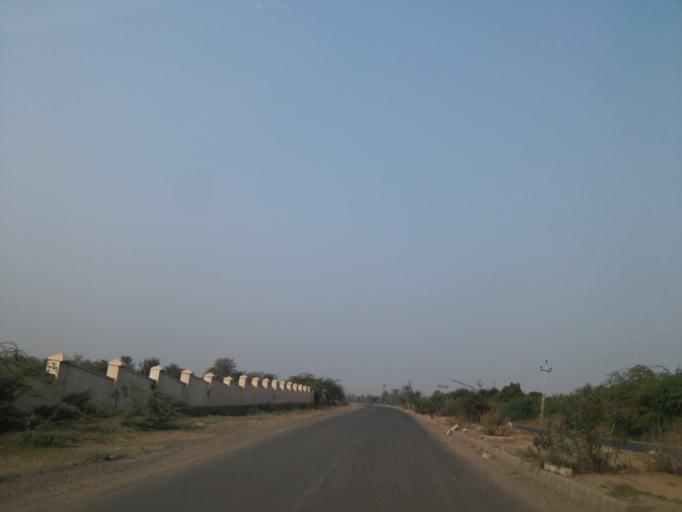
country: IN
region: Gujarat
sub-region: Kachchh
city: Bhuj
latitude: 23.2694
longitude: 69.6888
